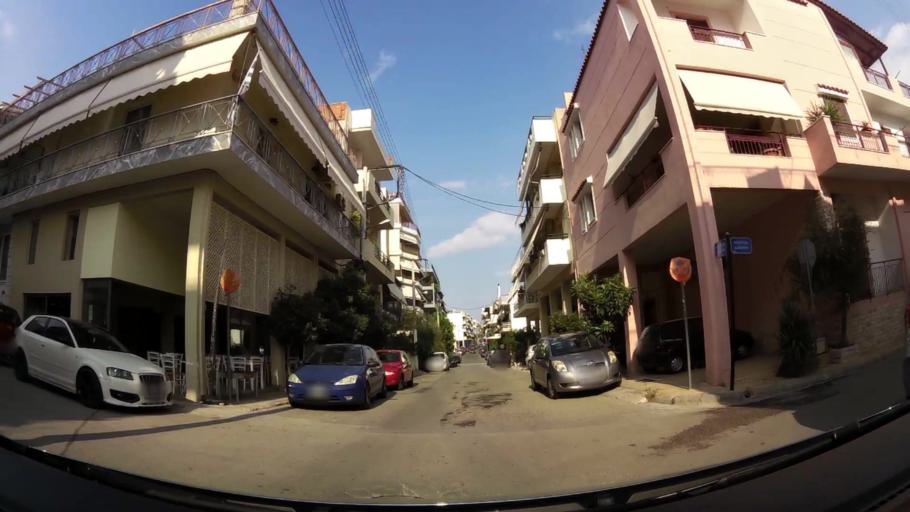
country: GR
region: Attica
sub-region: Nomarchia Athinas
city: Petroupolis
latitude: 38.0474
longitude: 23.6942
